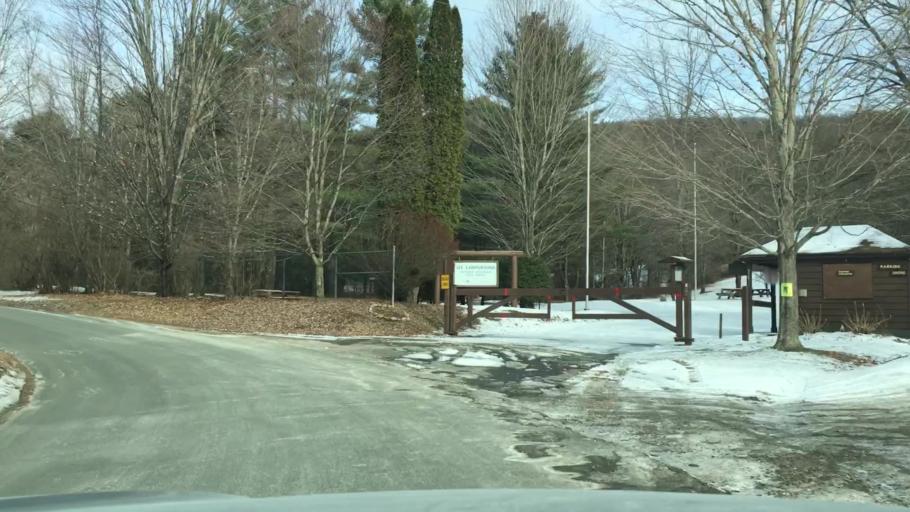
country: US
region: Massachusetts
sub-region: Berkshire County
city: Lee
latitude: 42.3362
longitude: -73.2340
